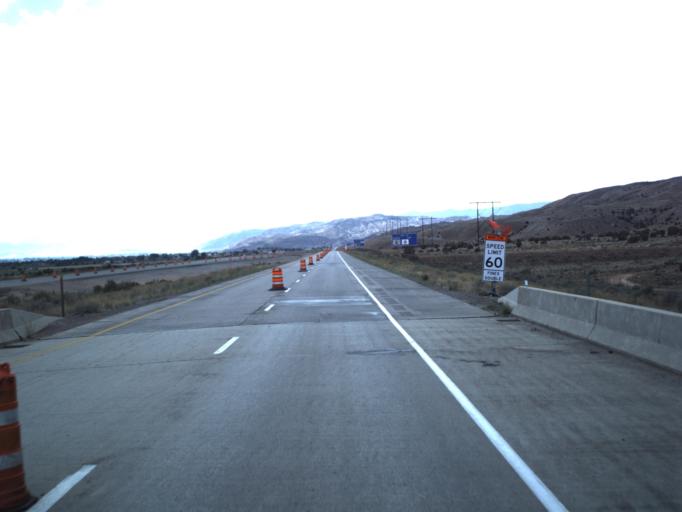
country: US
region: Utah
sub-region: Sevier County
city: Richfield
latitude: 38.8132
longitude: -112.0548
